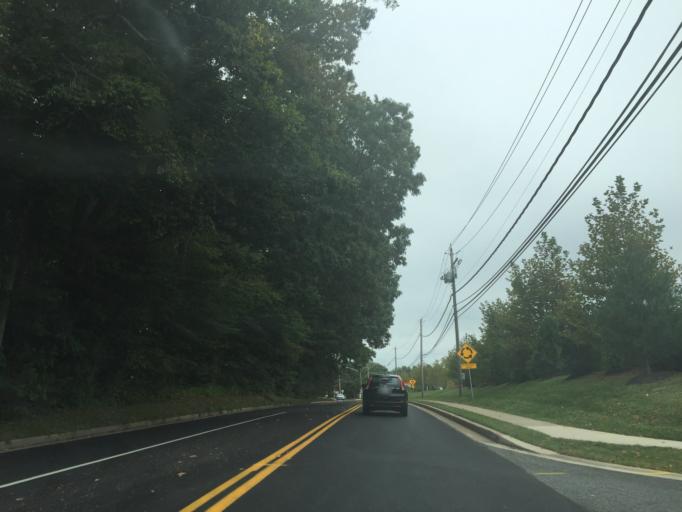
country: US
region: Maryland
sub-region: Harford County
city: South Bel Air
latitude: 39.5105
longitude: -76.3465
